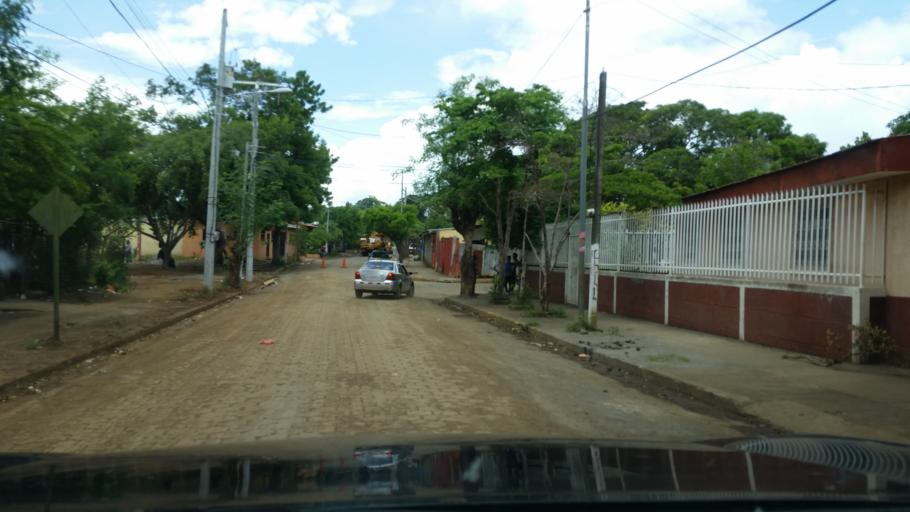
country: NI
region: Managua
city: Managua
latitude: 12.1307
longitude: -86.2600
